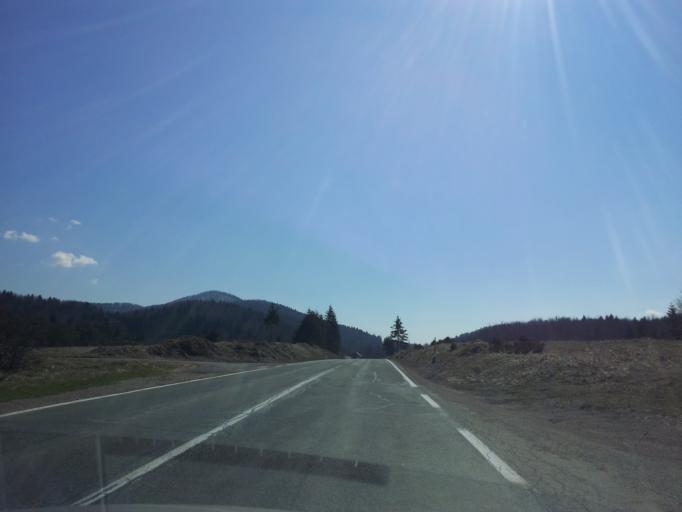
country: HR
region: Licko-Senjska
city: Jezerce
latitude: 44.8112
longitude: 15.6818
